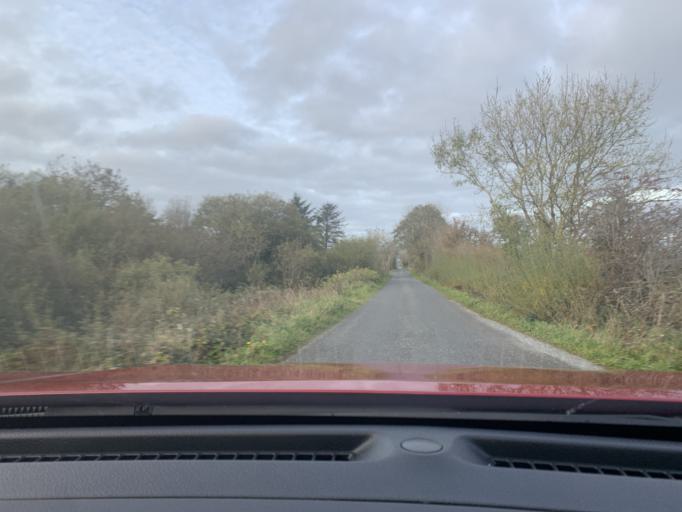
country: IE
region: Connaught
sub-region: Roscommon
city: Ballaghaderreen
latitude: 53.9904
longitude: -8.6117
